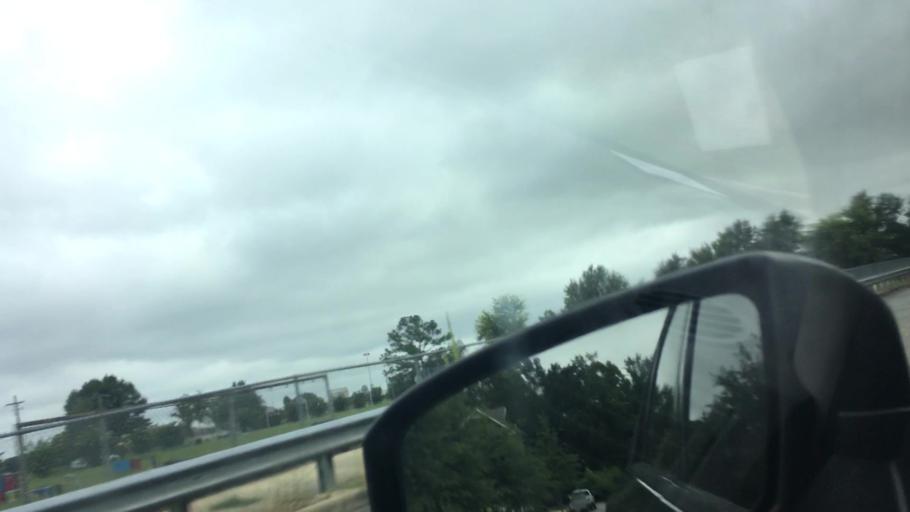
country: US
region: Alabama
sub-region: Tuscaloosa County
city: Tuscaloosa
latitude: 33.1908
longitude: -87.5193
